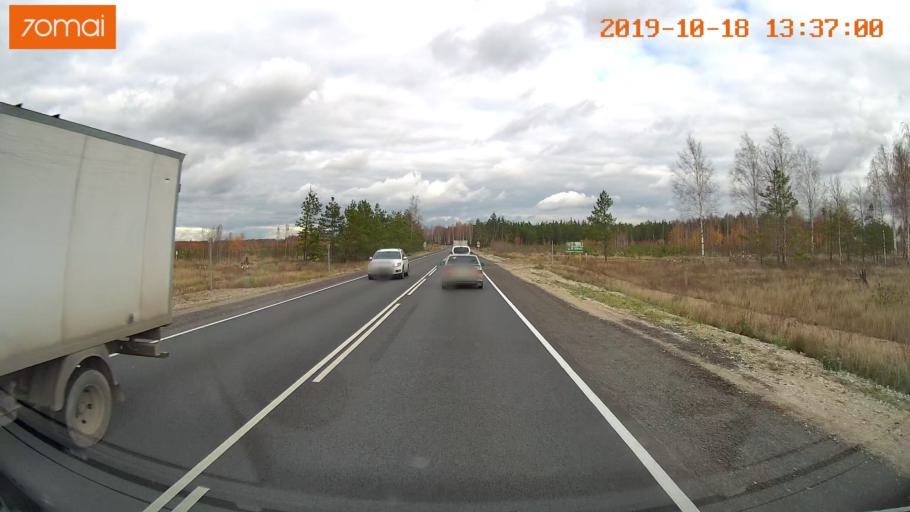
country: RU
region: Rjazan
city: Solotcha
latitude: 54.8757
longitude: 39.9902
